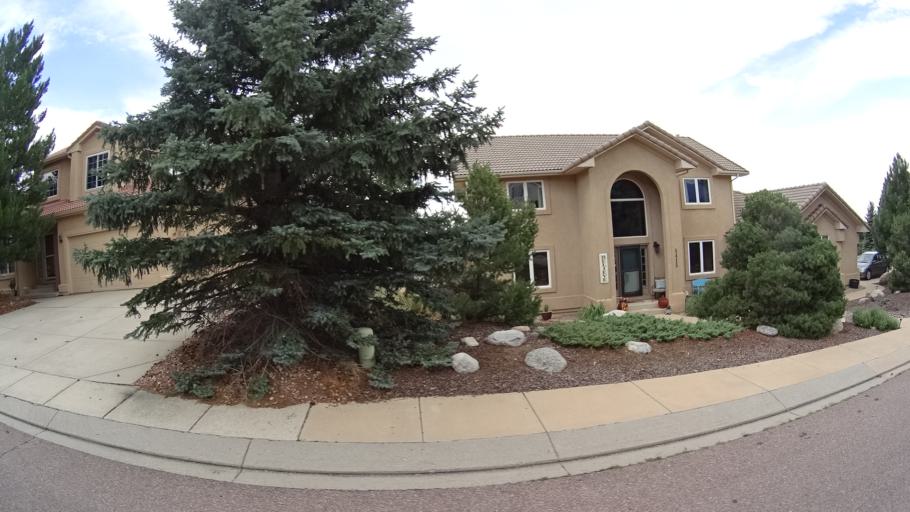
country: US
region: Colorado
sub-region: El Paso County
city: Colorado Springs
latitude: 38.9095
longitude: -104.8362
